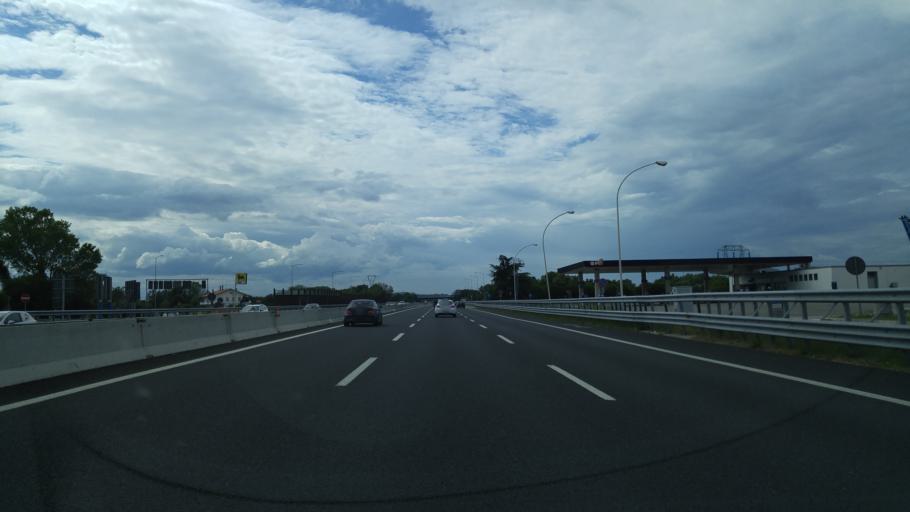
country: IT
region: Emilia-Romagna
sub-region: Provincia di Rimini
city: Coriano
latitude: 43.9944
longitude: 12.6197
